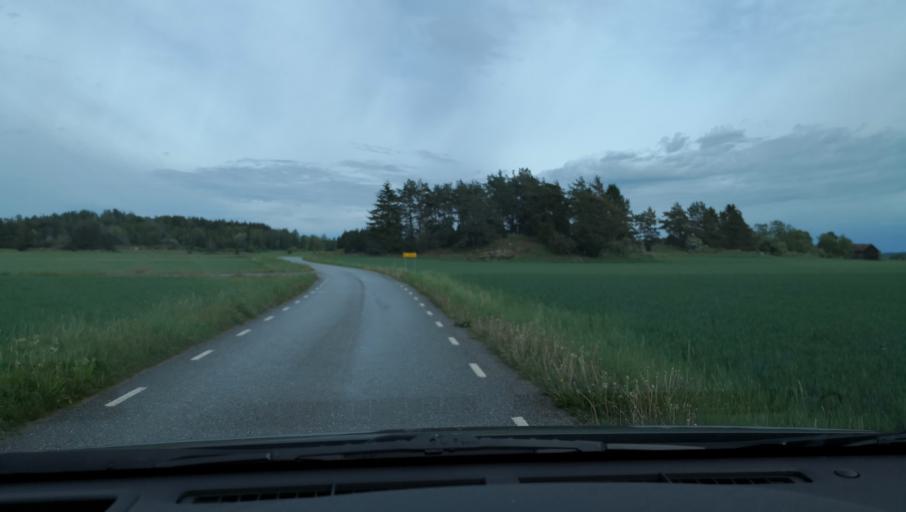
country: SE
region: Uppsala
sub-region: Enkopings Kommun
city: Orsundsbro
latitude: 59.7066
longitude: 17.3746
